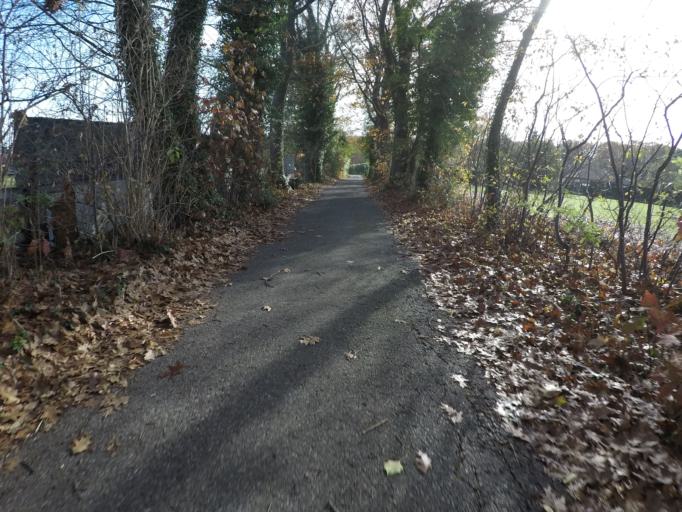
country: BE
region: Flanders
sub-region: Provincie Vlaams-Brabant
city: Begijnendijk
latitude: 51.0285
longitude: 4.7806
